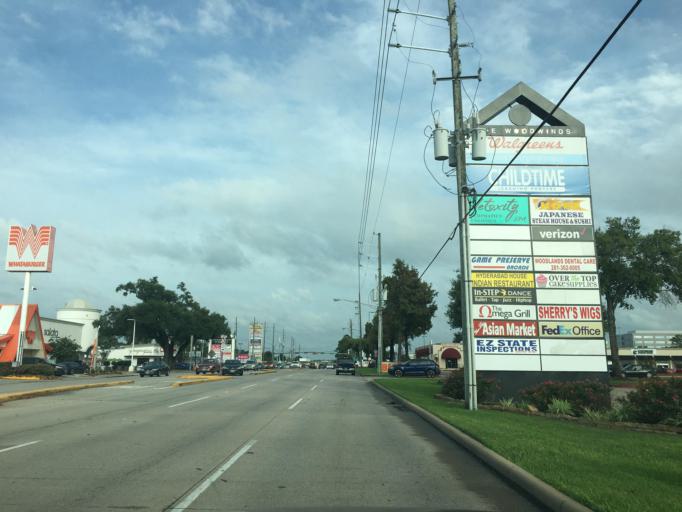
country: US
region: Texas
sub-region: Montgomery County
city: Oak Ridge North
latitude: 30.1266
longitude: -95.4489
